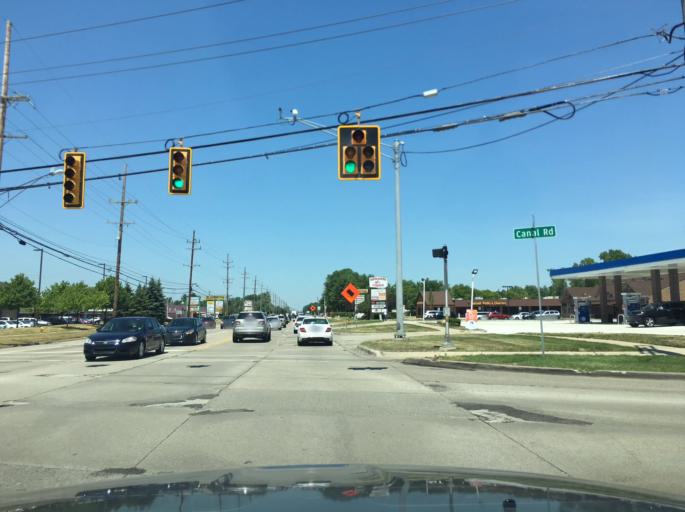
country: US
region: Michigan
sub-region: Macomb County
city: Clinton
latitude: 42.6052
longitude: -82.9526
